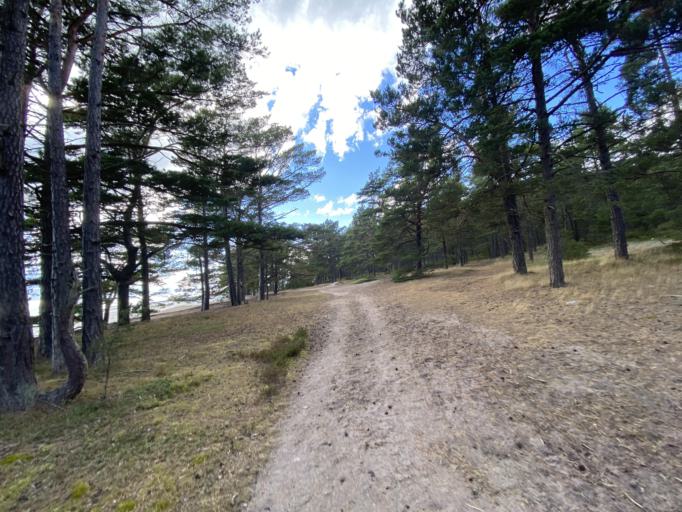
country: SE
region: Stockholm
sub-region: Varmdo Kommun
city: Holo
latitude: 59.2787
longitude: 18.9090
